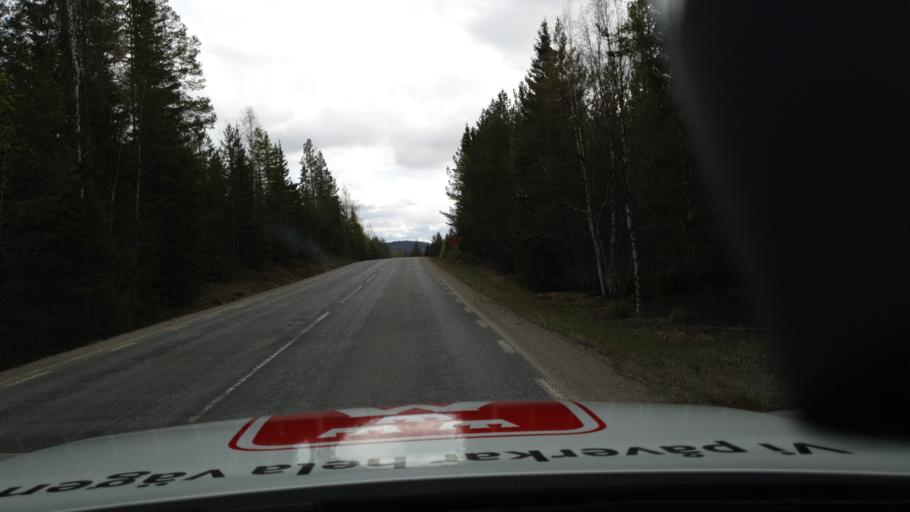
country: SE
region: Jaemtland
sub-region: Braecke Kommun
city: Braecke
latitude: 62.7633
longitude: 15.4421
